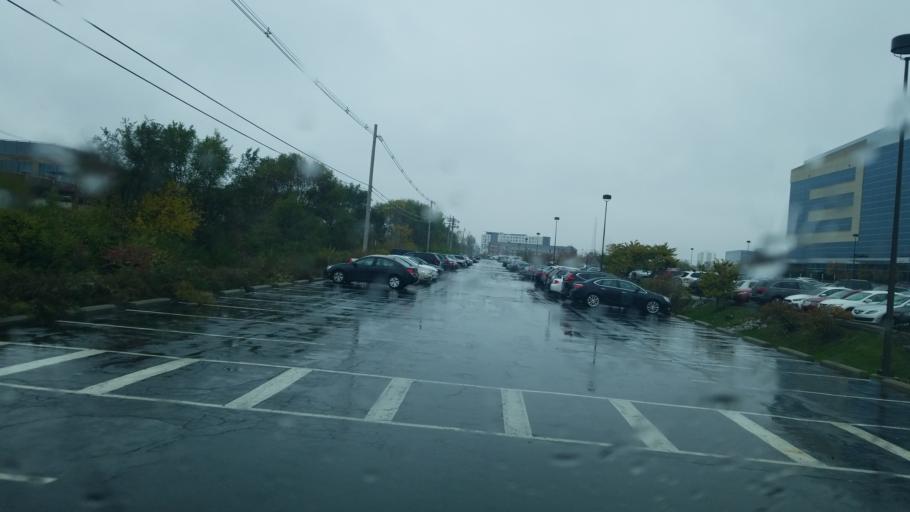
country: US
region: Ohio
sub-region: Franklin County
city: Grandview Heights
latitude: 39.9796
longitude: -83.0242
